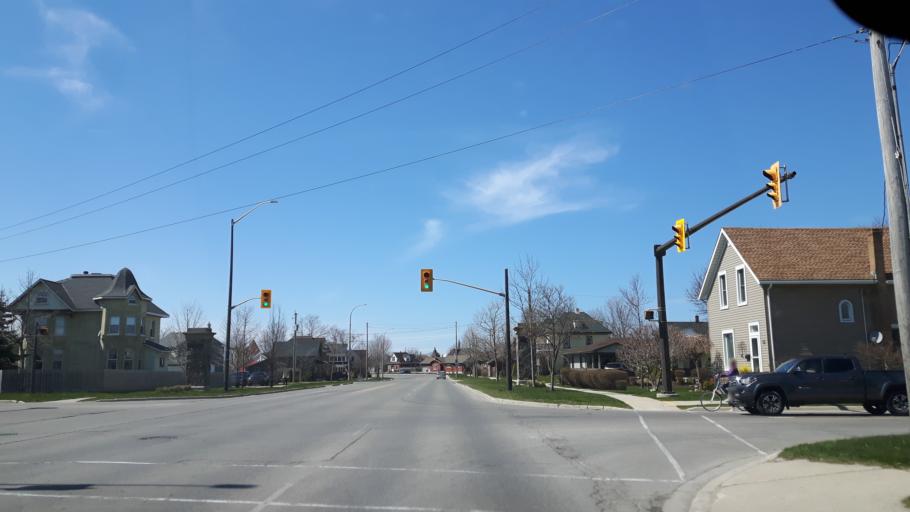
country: CA
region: Ontario
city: Goderich
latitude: 43.7392
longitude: -81.7026
